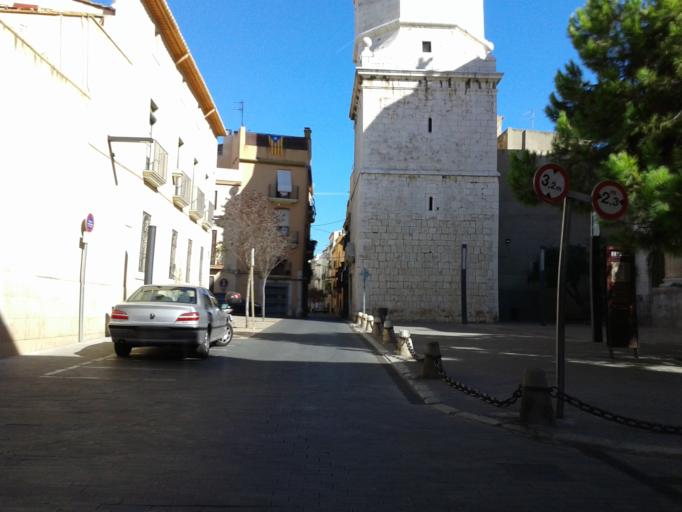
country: ES
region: Catalonia
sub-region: Provincia de Barcelona
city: Vilanova i la Geltru
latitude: 41.2269
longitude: 1.7232
